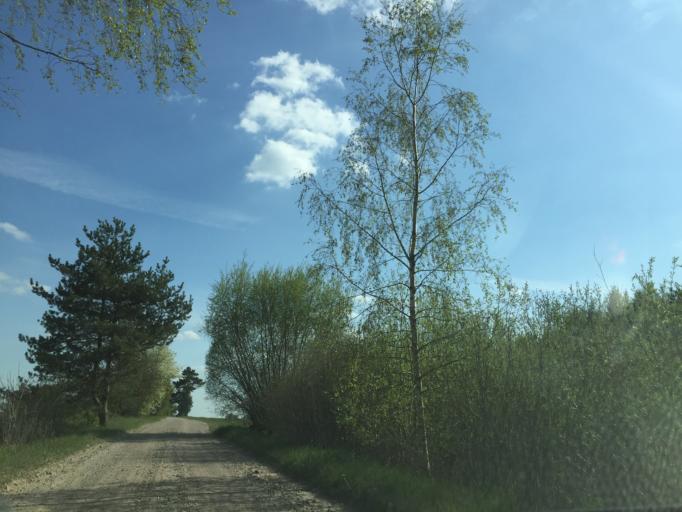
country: LV
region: Lecava
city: Iecava
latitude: 56.5028
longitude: 24.3182
